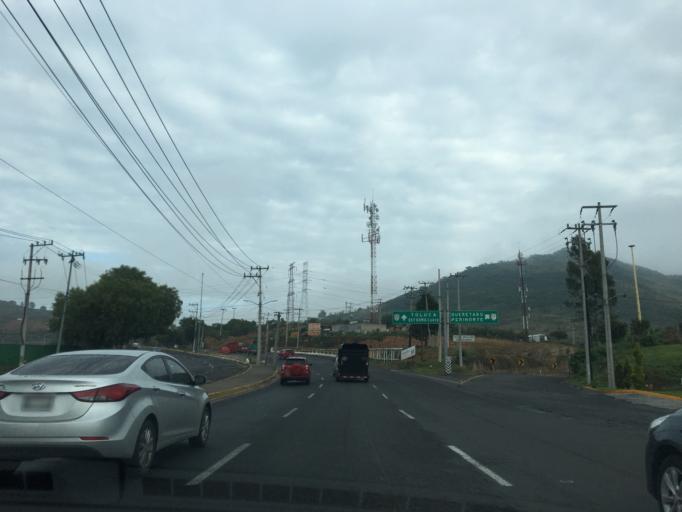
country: MX
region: Mexico
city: Ciudad Lopez Mateos
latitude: 19.5459
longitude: -99.2761
